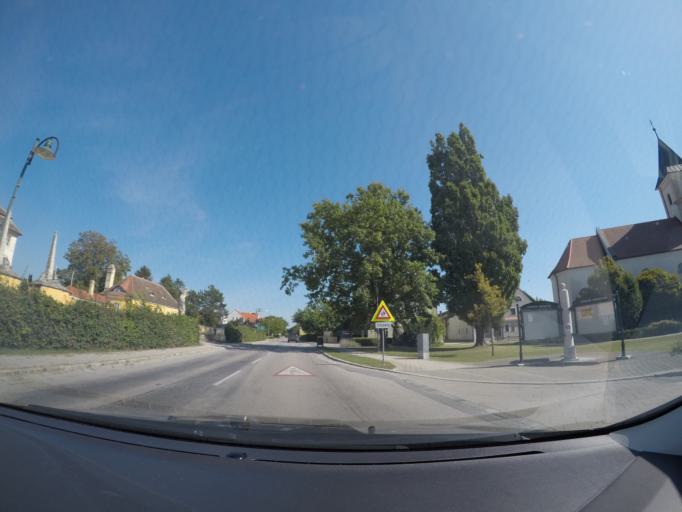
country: AT
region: Lower Austria
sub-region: Politischer Bezirk Baden
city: Seibersdorf
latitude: 47.9587
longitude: 16.5193
